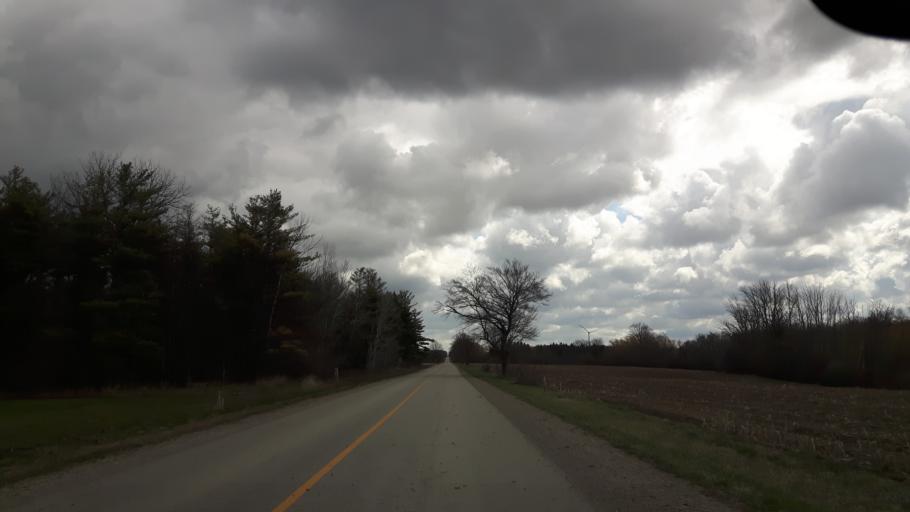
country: CA
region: Ontario
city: Bluewater
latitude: 43.5434
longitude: -81.6988
